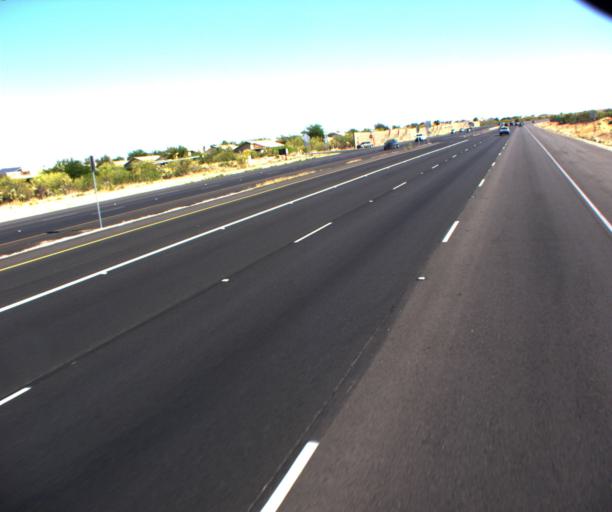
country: US
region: Arizona
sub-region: Pima County
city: Catalina
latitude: 32.4453
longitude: -110.9337
